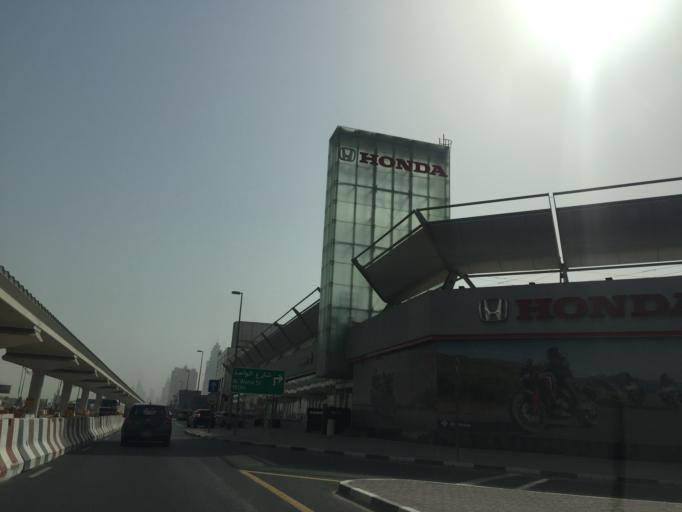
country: AE
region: Dubai
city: Dubai
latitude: 25.1678
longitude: 55.2390
